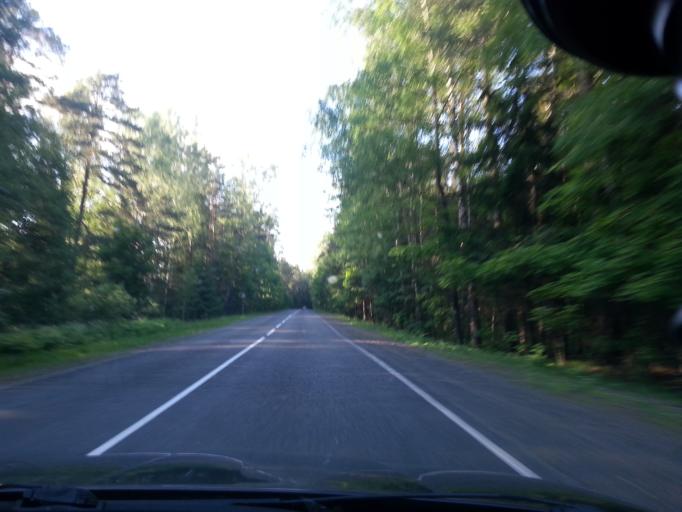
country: BY
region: Minsk
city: Narach
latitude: 54.9350
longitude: 26.5636
